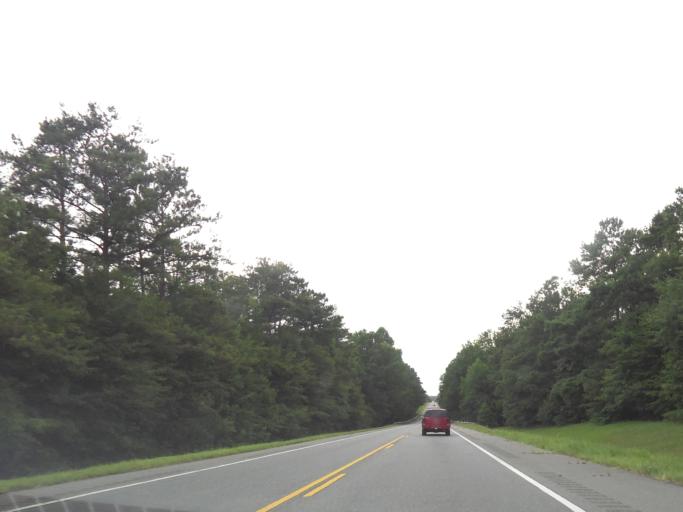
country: US
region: Georgia
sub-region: Bibb County
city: West Point
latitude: 32.7987
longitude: -83.7841
